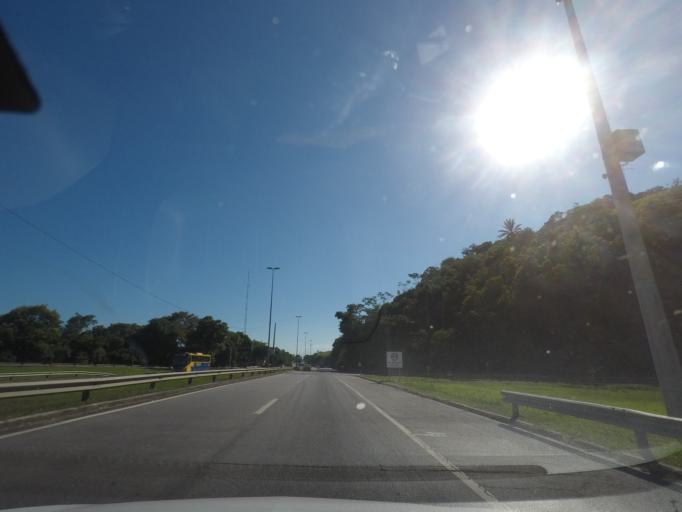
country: BR
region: Rio de Janeiro
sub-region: Guapimirim
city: Guapimirim
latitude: -22.6579
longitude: -43.0900
